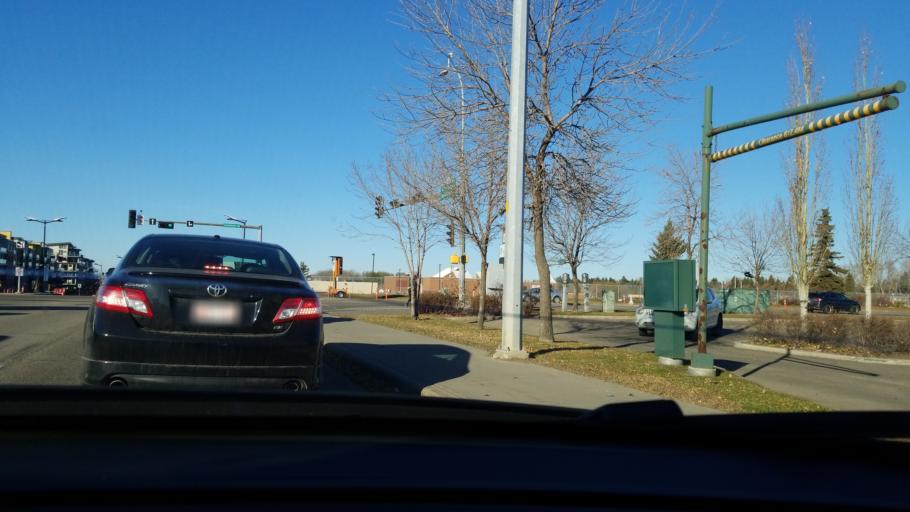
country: CA
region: Alberta
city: Sherwood Park
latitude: 53.5281
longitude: -113.2949
